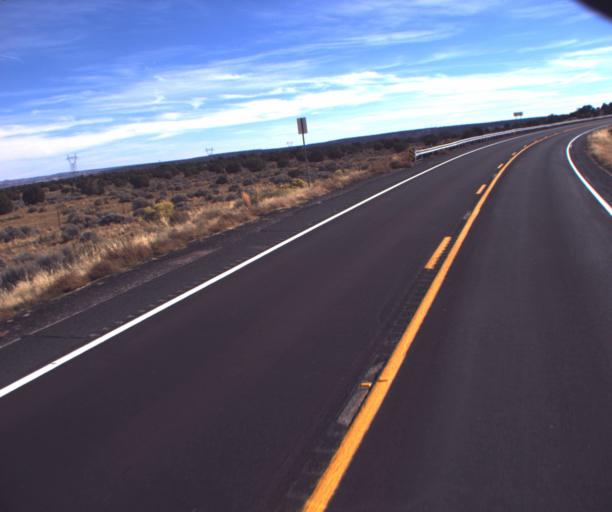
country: US
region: Arizona
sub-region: Coconino County
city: Kaibito
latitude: 36.6142
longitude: -110.9270
